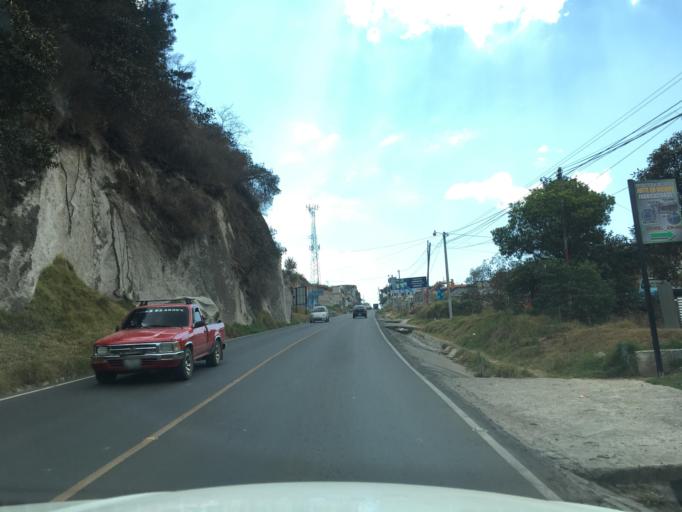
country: GT
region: Quetzaltenango
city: Olintepeque
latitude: 14.8808
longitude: -91.5143
